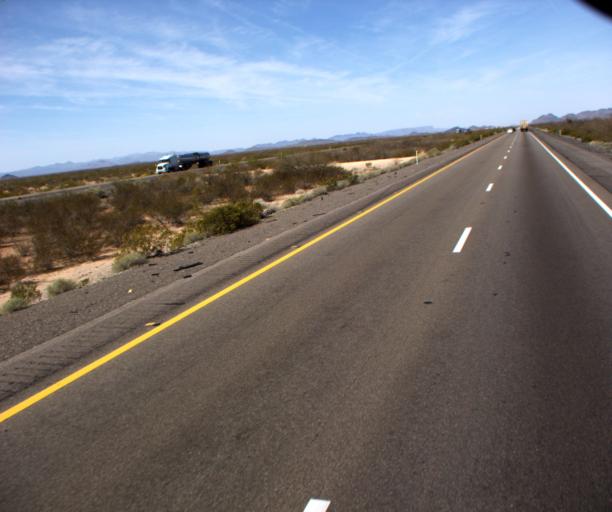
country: US
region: Arizona
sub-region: La Paz County
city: Salome
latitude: 33.5902
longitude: -113.4915
